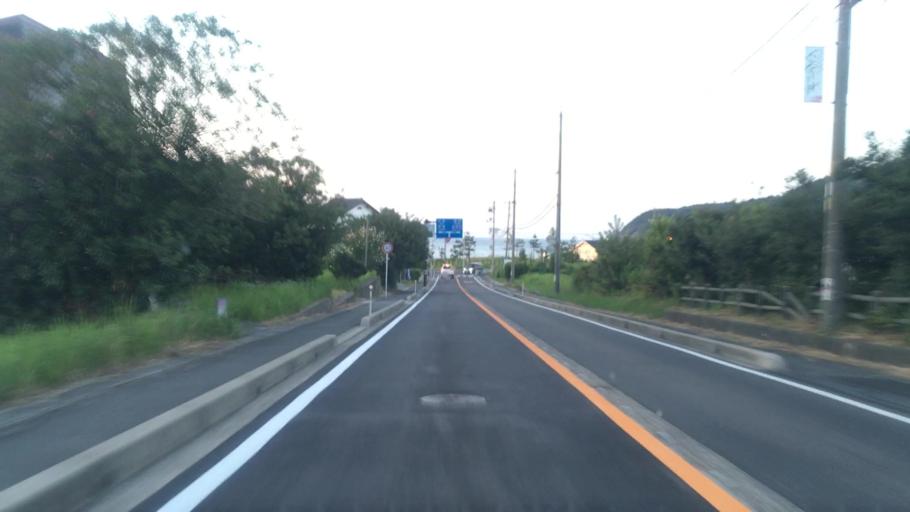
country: JP
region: Tottori
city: Tottori
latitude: 35.5893
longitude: 134.3327
